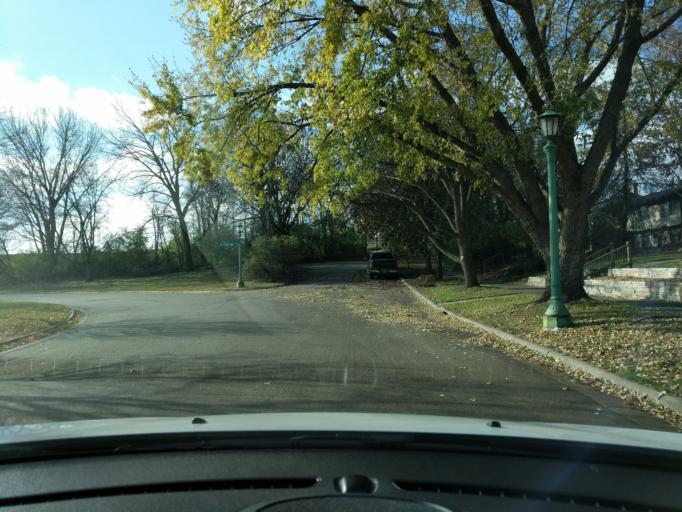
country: US
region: Minnesota
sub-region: Ramsey County
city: Lauderdale
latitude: 44.9761
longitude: -93.1959
